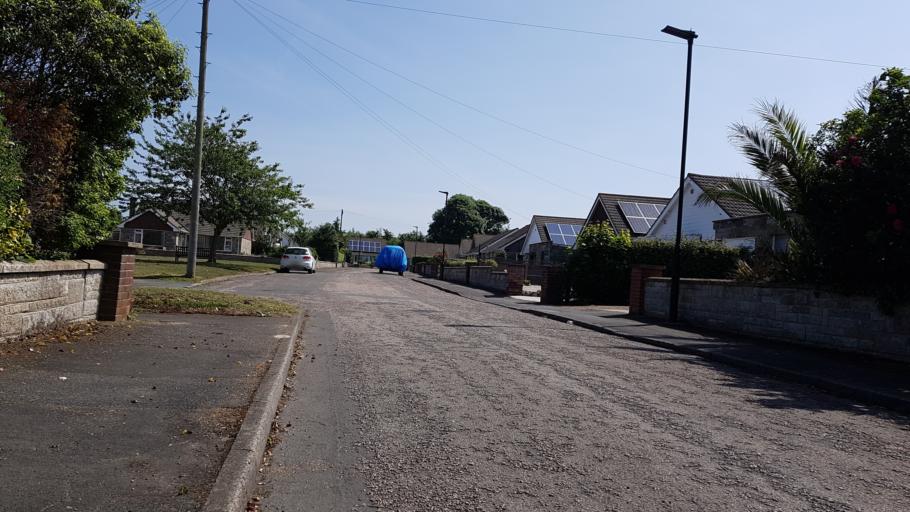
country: GB
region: England
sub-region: Isle of Wight
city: Northwood
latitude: 50.7514
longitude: -1.3115
